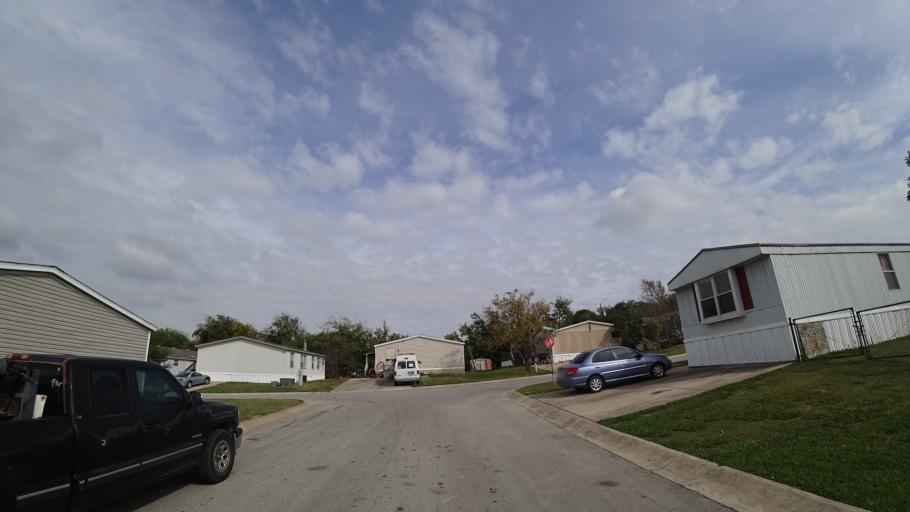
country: US
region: Texas
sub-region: Williamson County
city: Round Rock
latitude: 30.4877
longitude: -97.6891
